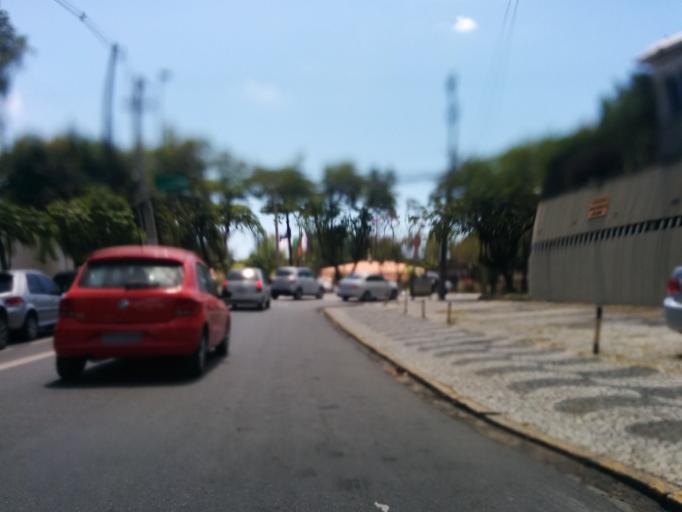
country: BR
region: Pernambuco
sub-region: Recife
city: Recife
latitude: -8.0469
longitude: -34.8925
